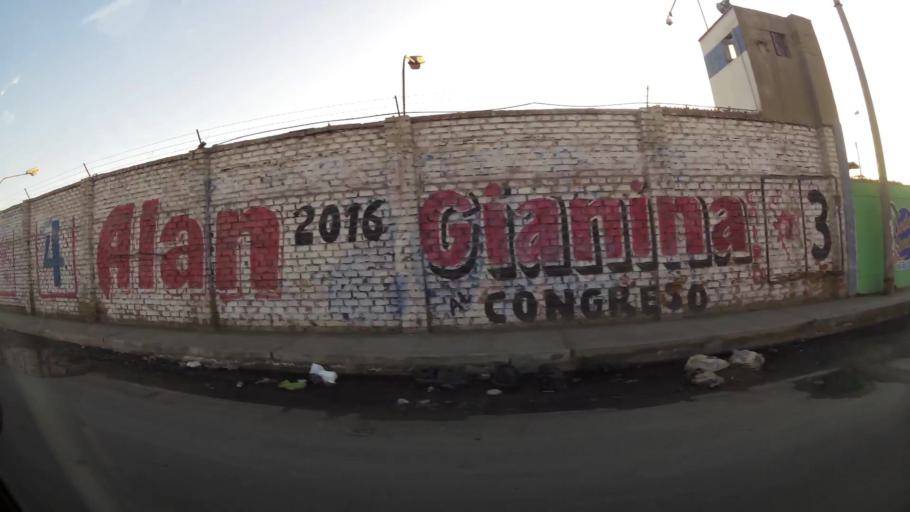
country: PE
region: Ica
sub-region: Provincia de Ica
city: Ica
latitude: -14.0805
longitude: -75.7219
